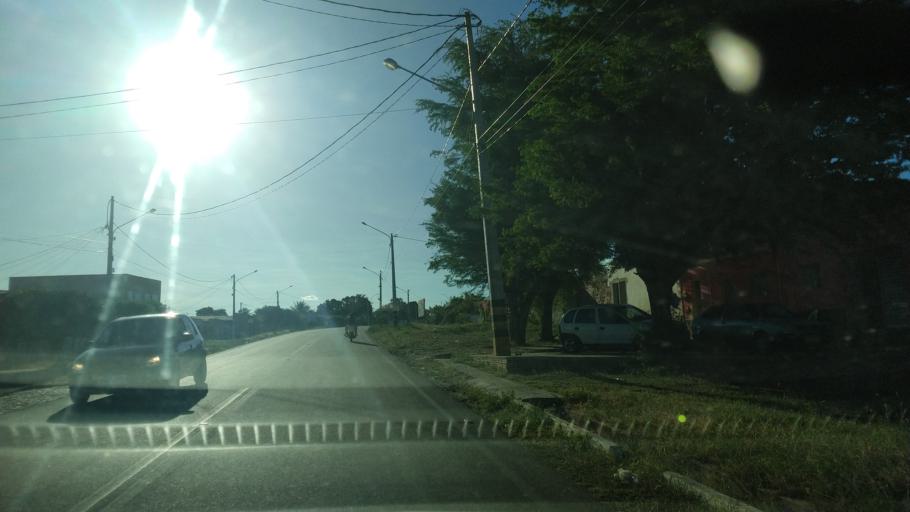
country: BR
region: Rio Grande do Norte
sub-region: Sao Jose Do Campestre
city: Sao Jose do Campestre
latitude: -6.3132
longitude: -35.7143
